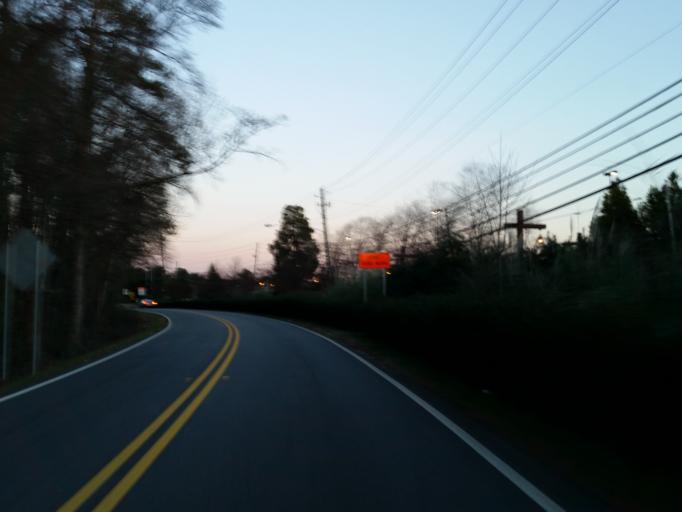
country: US
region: Georgia
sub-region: Cobb County
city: Vinings
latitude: 33.8397
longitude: -84.4823
